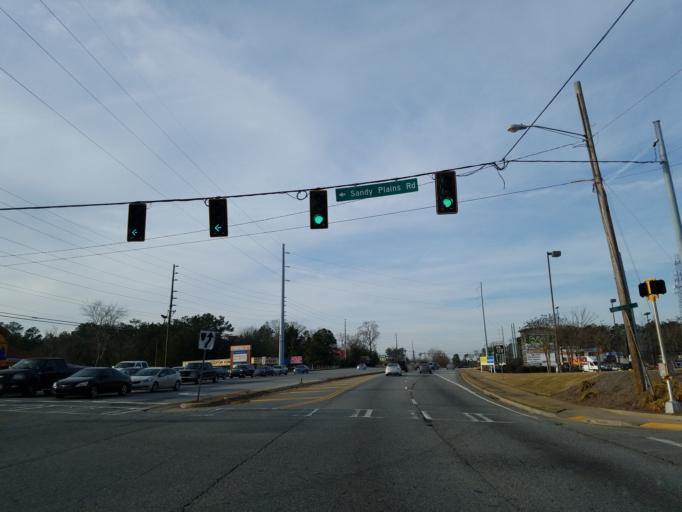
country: US
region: Georgia
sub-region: Fulton County
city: Roswell
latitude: 34.0641
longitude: -84.4234
